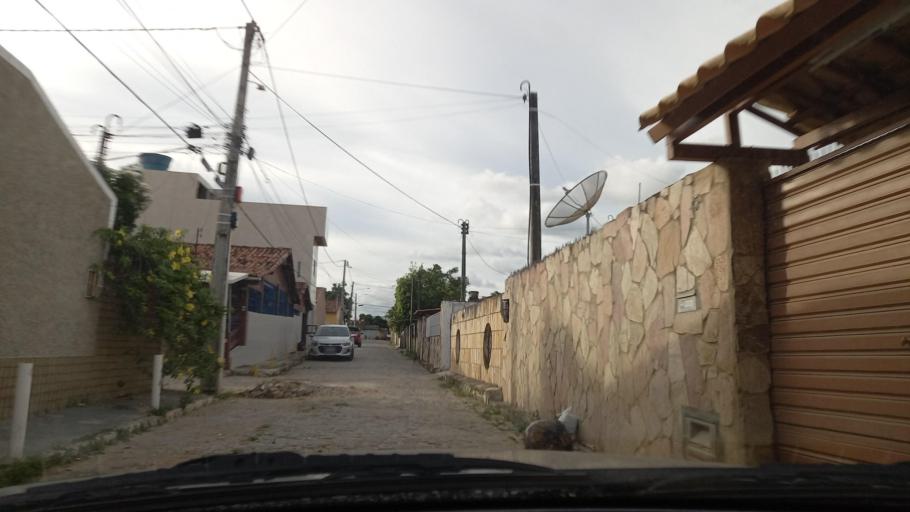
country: BR
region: Pernambuco
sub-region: Gravata
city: Gravata
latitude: -8.1996
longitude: -35.5595
